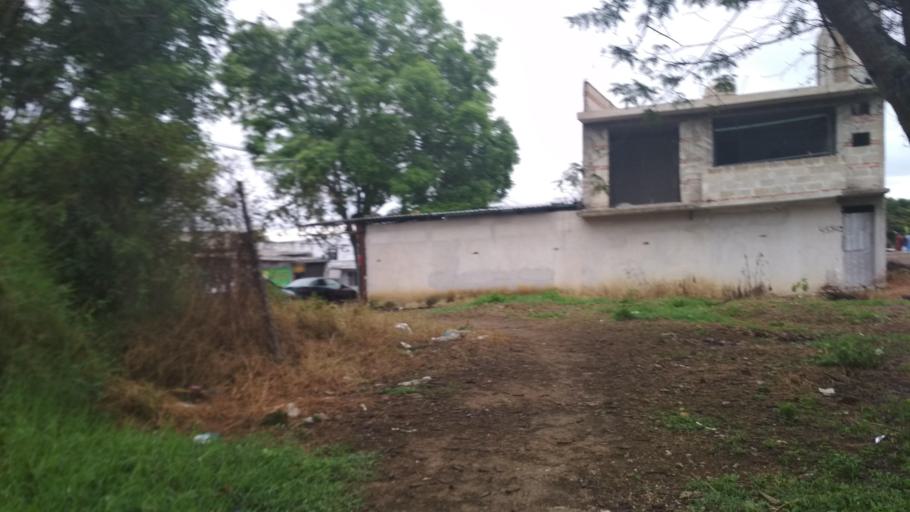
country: MX
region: Veracruz
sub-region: Emiliano Zapata
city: Las Trancas
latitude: 19.5069
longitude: -96.8683
